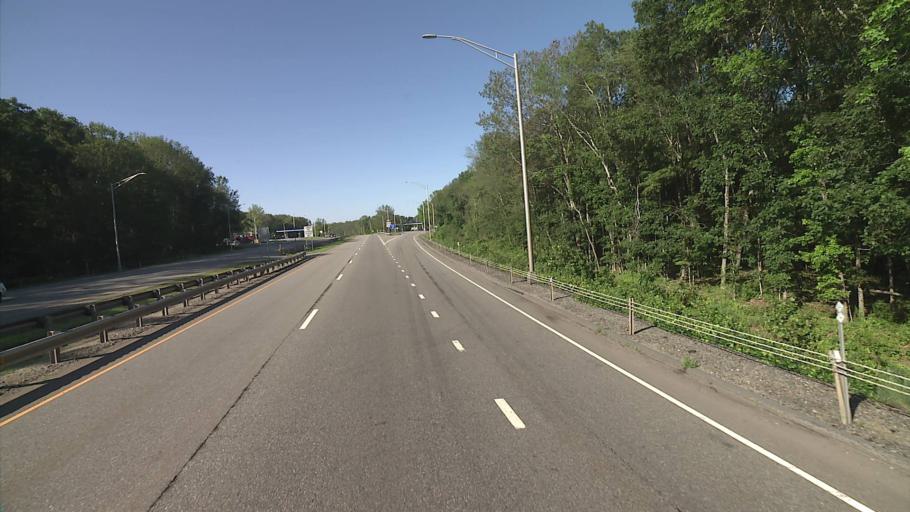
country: US
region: Connecticut
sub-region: Windham County
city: Wauregan
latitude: 41.7566
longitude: -71.8764
